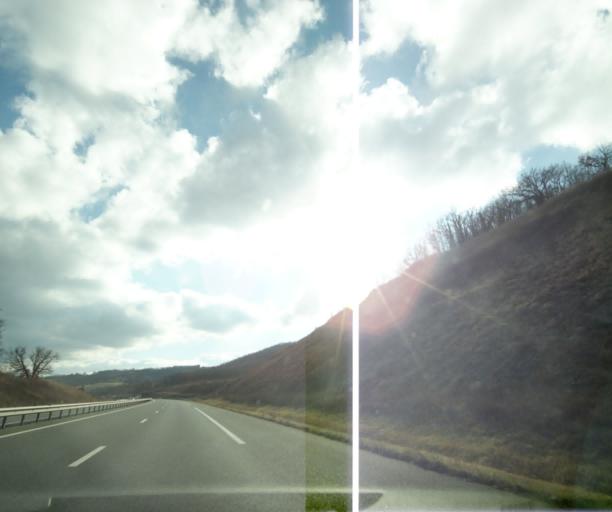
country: FR
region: Midi-Pyrenees
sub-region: Departement du Lot
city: Le Vigan
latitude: 44.7589
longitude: 1.5395
